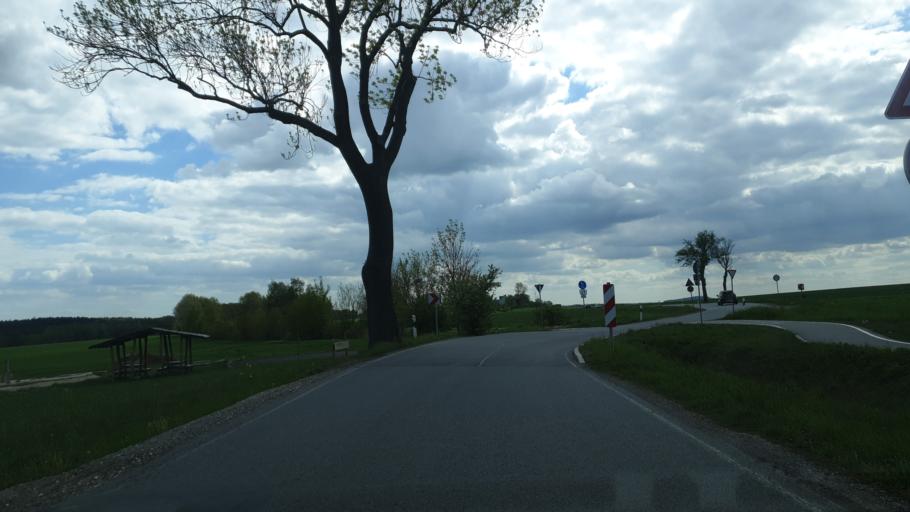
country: DE
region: Saxony
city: Lugau
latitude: 50.7564
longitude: 12.7687
